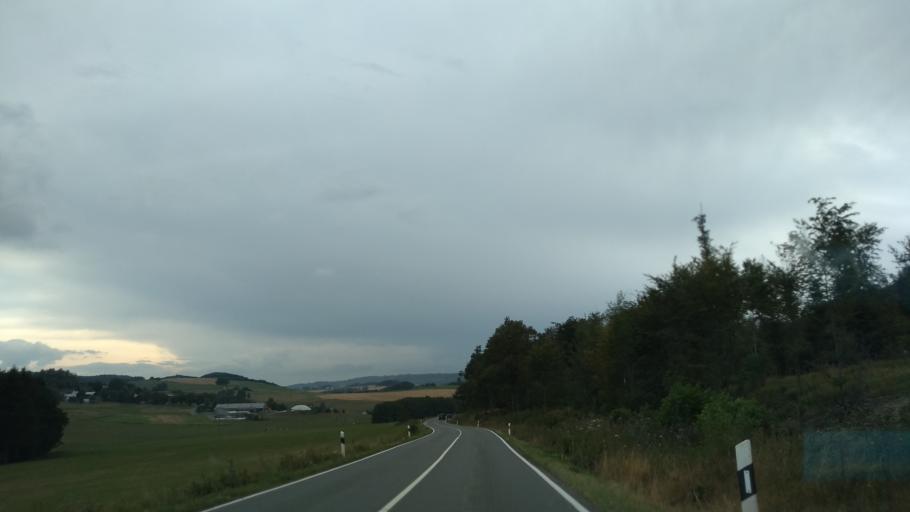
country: DE
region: North Rhine-Westphalia
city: Balve
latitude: 51.3047
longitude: 7.9152
